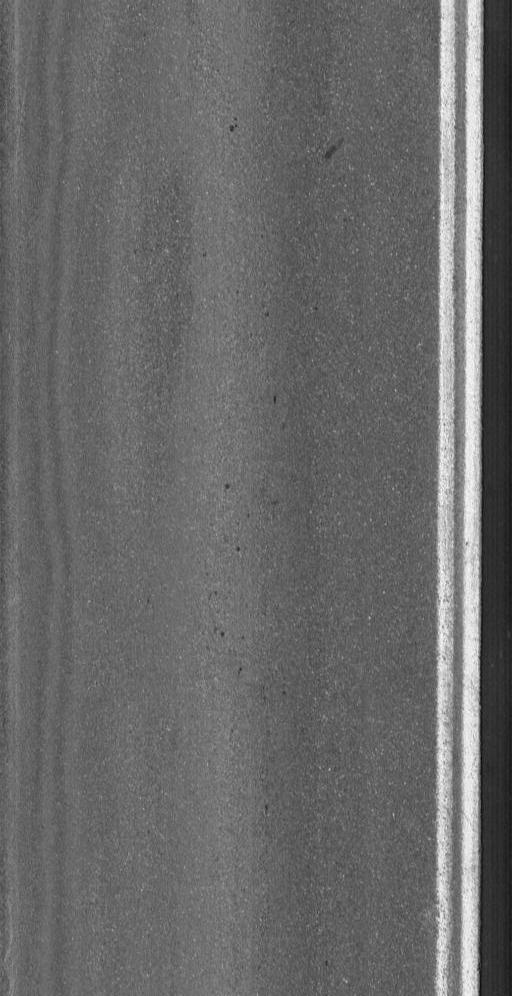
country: US
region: New Hampshire
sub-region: Grafton County
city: Hanover
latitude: 43.7184
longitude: -72.3093
